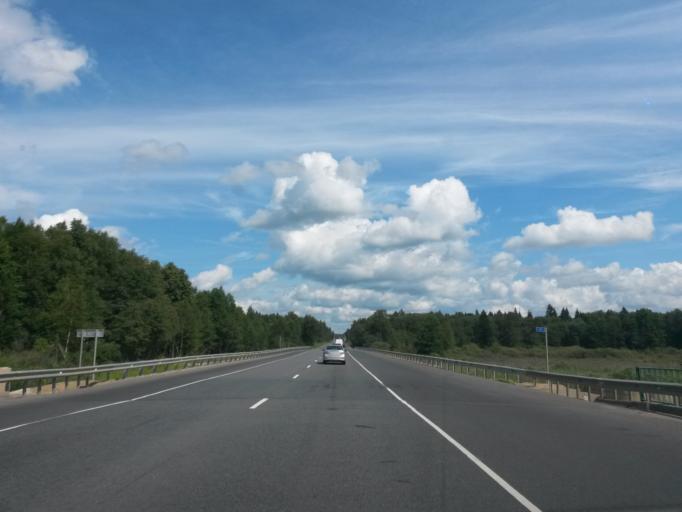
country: RU
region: Jaroslavl
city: Pereslavl'-Zalesskiy
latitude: 56.8314
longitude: 38.9156
